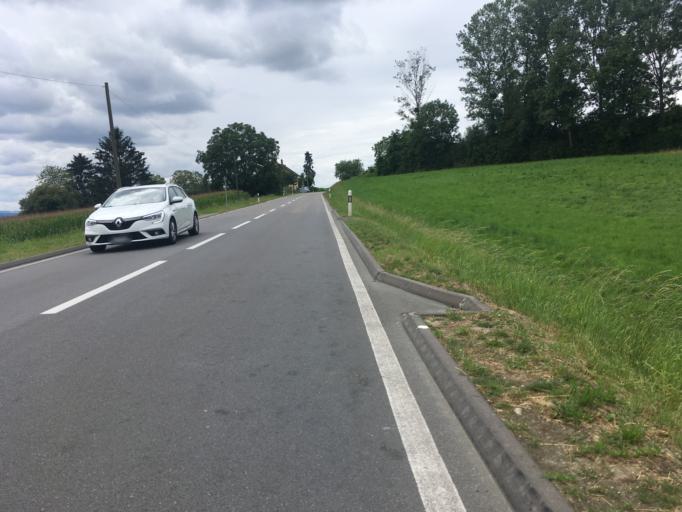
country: CH
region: Fribourg
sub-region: Broye District
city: Domdidier
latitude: 46.8857
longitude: 6.9791
